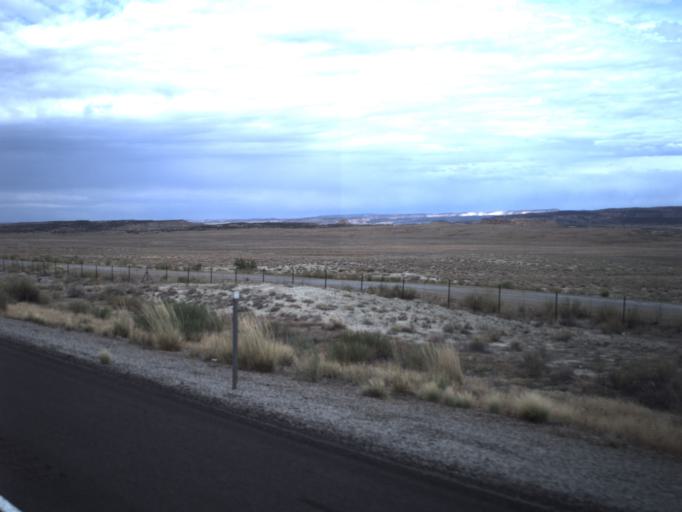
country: US
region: Colorado
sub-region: Mesa County
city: Loma
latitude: 39.0561
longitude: -109.2589
